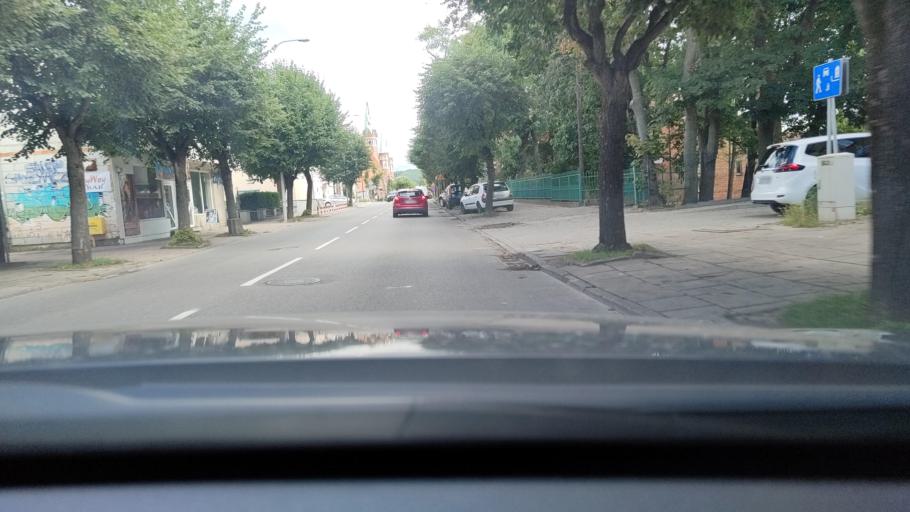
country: PL
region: Pomeranian Voivodeship
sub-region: Powiat wejherowski
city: Wejherowo
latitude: 54.5998
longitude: 18.2328
